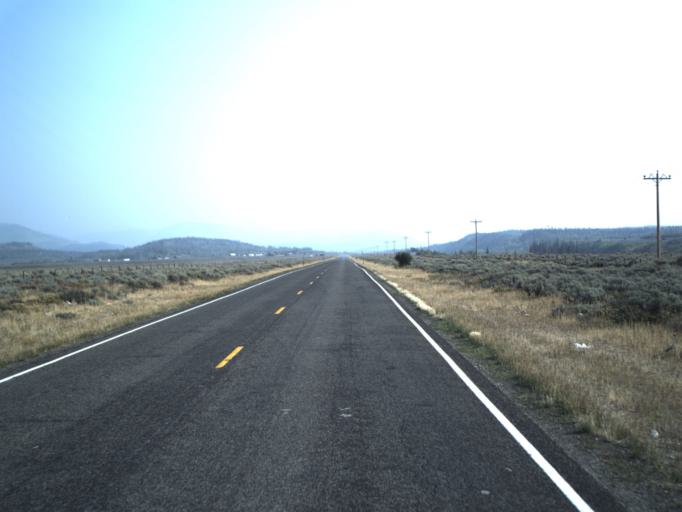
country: US
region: Wyoming
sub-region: Uinta County
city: Evanston
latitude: 40.9581
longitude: -110.8439
